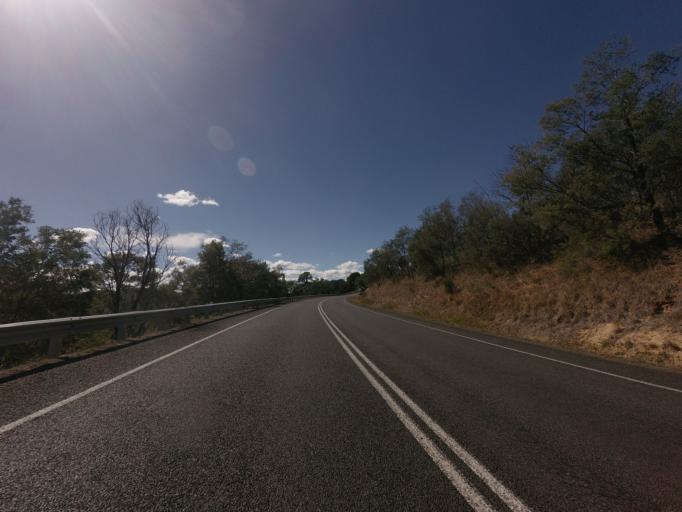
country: AU
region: Tasmania
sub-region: Break O'Day
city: St Helens
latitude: -41.7238
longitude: 147.8257
